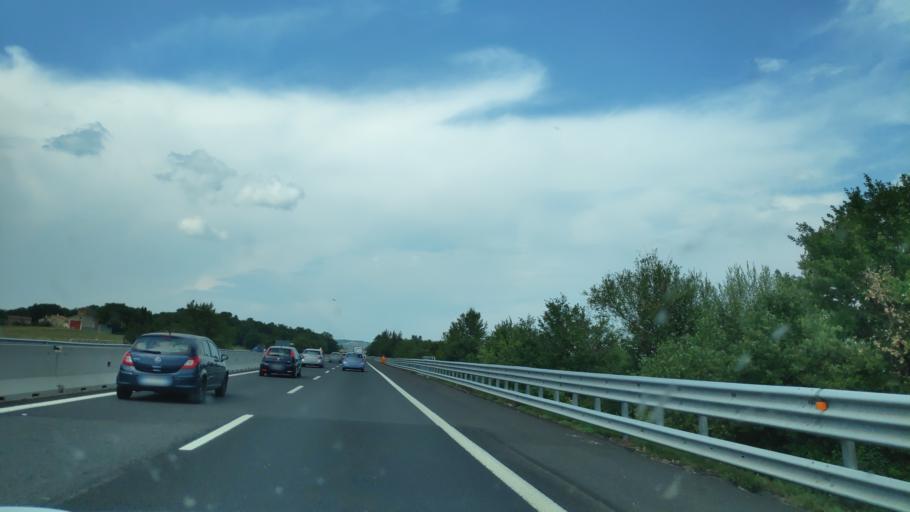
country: IT
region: Tuscany
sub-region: Province of Arezzo
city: Badia al Pino
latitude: 43.3777
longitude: 11.7567
